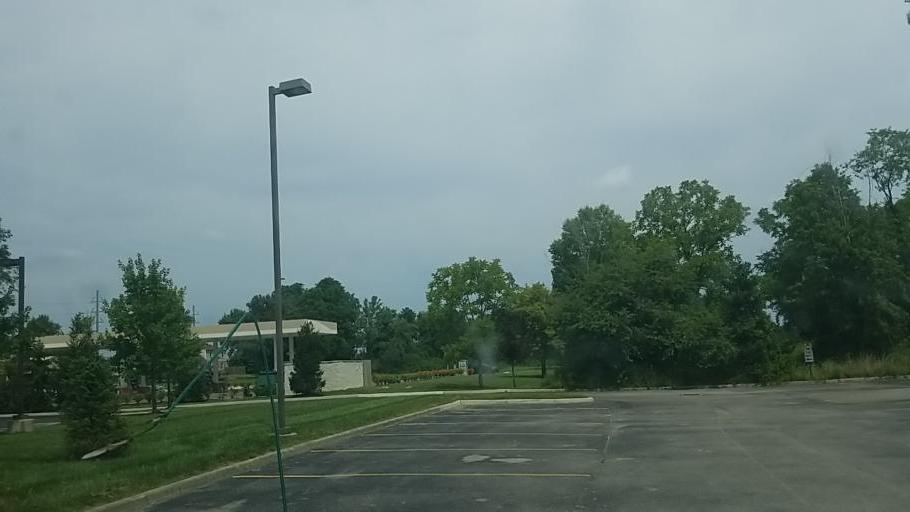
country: US
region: Ohio
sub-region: Franklin County
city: Gahanna
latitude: 40.0662
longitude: -82.8615
